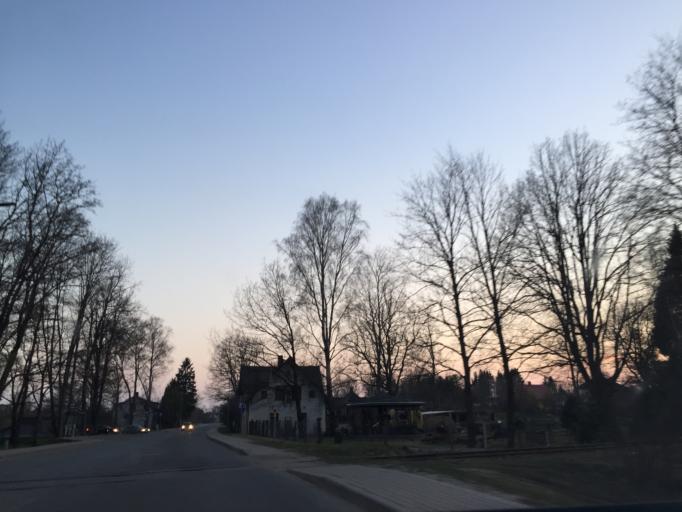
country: LV
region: Valkas Rajons
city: Valka
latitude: 57.7693
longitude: 26.0122
